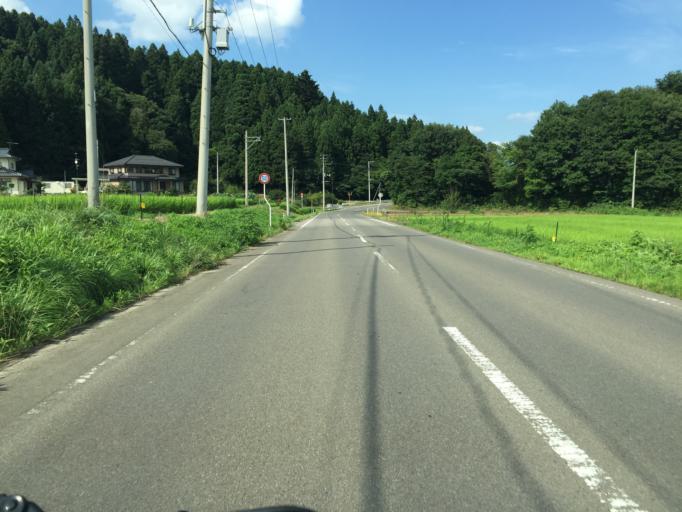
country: JP
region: Fukushima
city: Fukushima-shi
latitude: 37.7717
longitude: 140.3653
